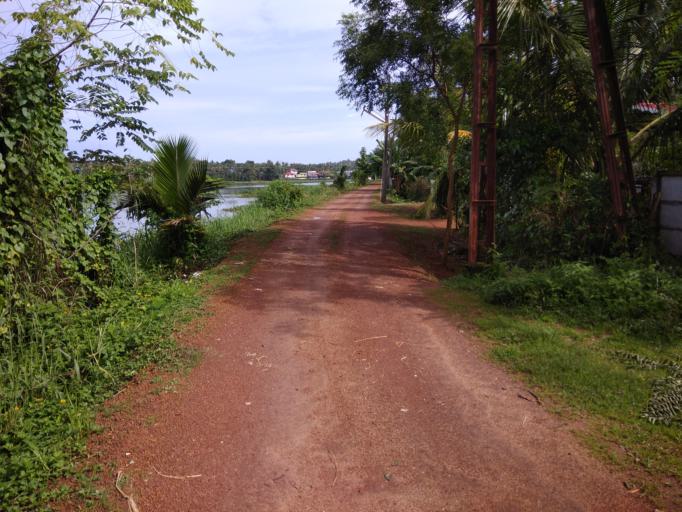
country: IN
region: Kerala
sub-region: Thrissur District
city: Trichur
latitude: 10.5342
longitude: 76.1779
